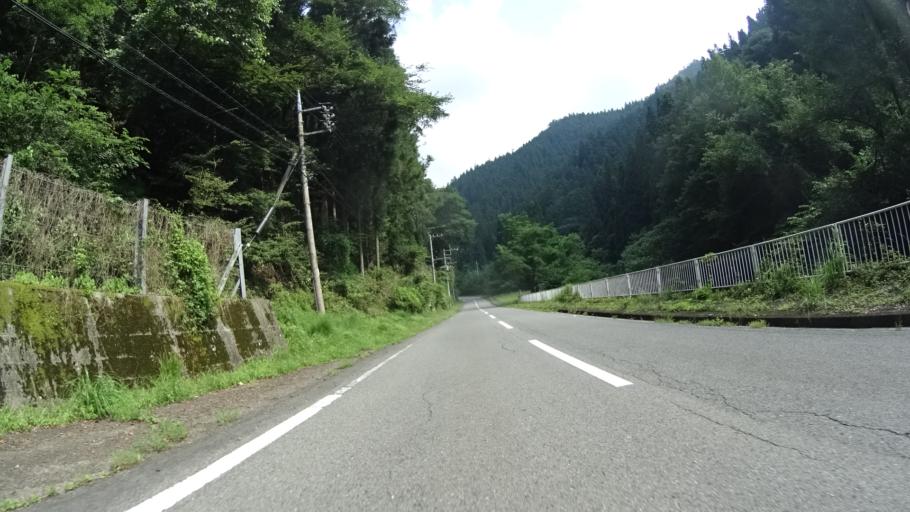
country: JP
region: Gunma
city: Tomioka
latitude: 36.0782
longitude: 138.8250
